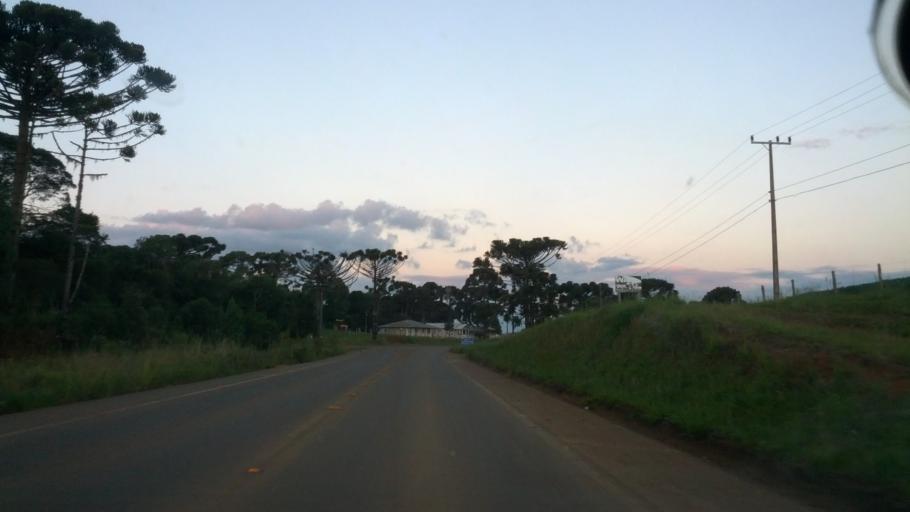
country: BR
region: Rio Grande do Sul
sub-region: Vacaria
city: Estrela
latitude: -27.8957
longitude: -50.7703
